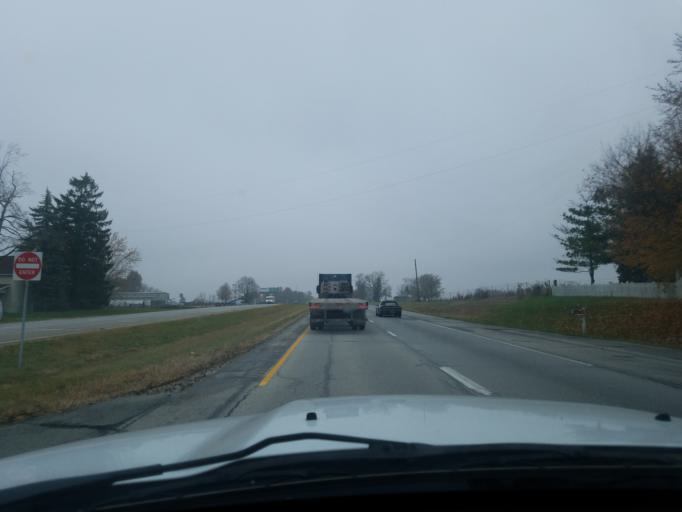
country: US
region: Indiana
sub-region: Hamilton County
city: Sheridan
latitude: 40.1388
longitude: -86.1278
